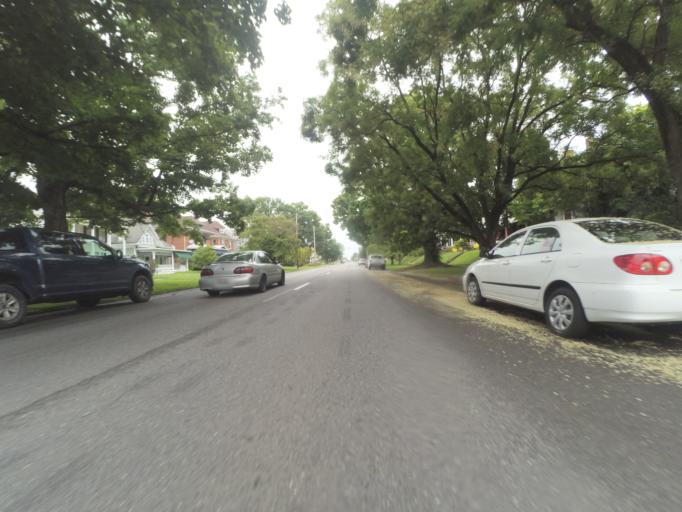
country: US
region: West Virginia
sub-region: Cabell County
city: Huntington
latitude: 38.4180
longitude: -82.4515
